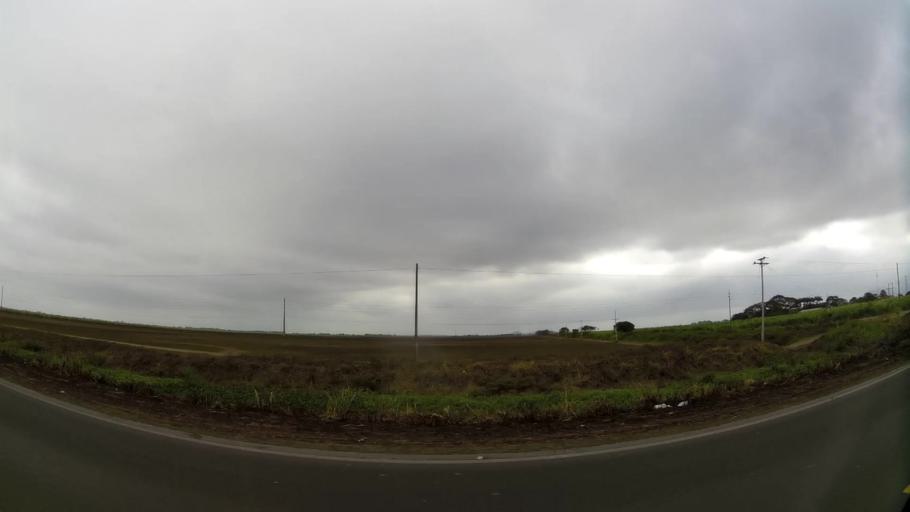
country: EC
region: Guayas
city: Coronel Marcelino Mariduena
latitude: -2.3443
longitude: -79.6345
